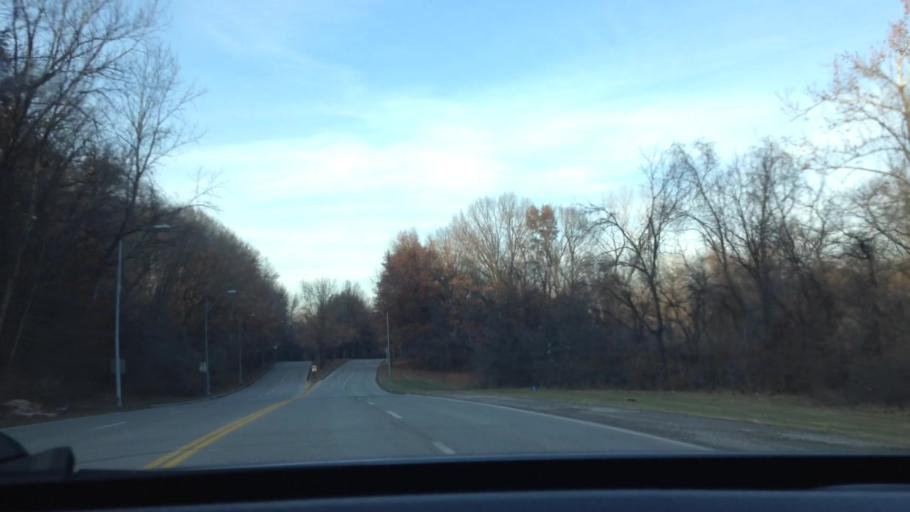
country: US
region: Missouri
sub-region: Clay County
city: North Kansas City
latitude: 39.1561
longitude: -94.5168
